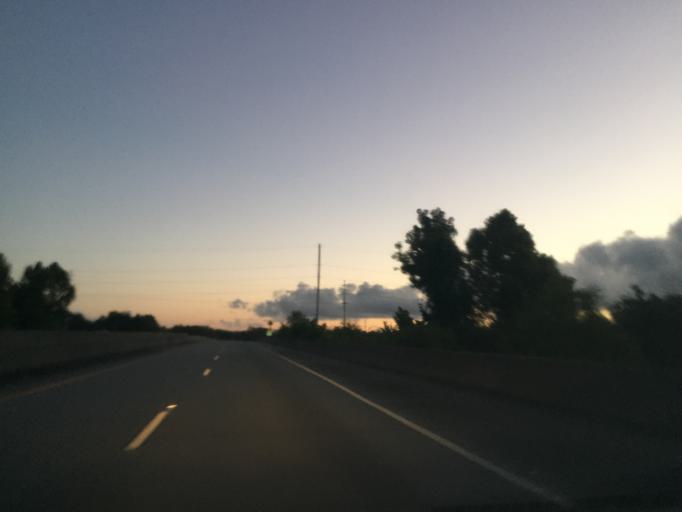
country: US
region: Georgia
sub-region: Chatham County
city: Savannah
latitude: 32.0716
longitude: -81.0735
